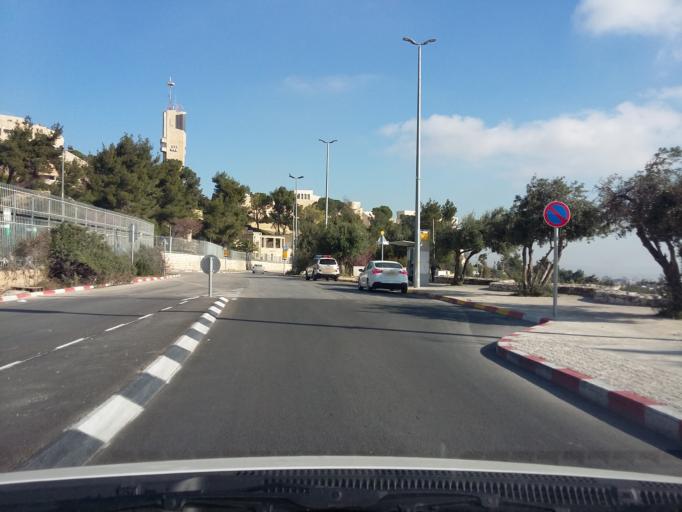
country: PS
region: West Bank
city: East Jerusalem
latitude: 31.7902
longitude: 35.2472
